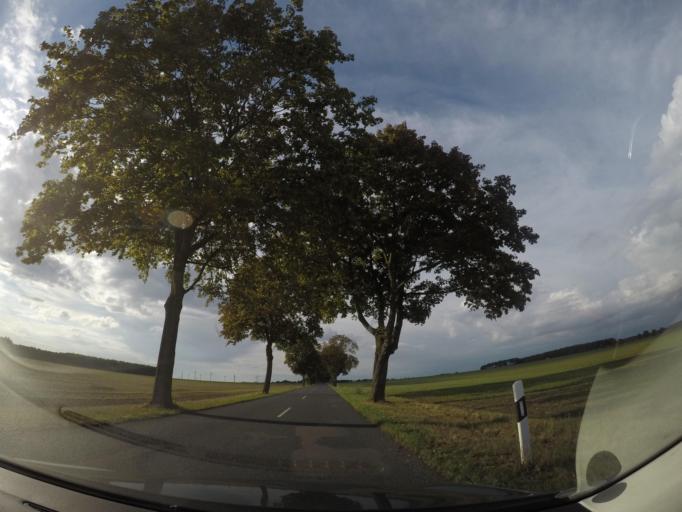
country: DE
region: Saxony-Anhalt
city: Kusey
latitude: 52.5691
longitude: 11.1259
